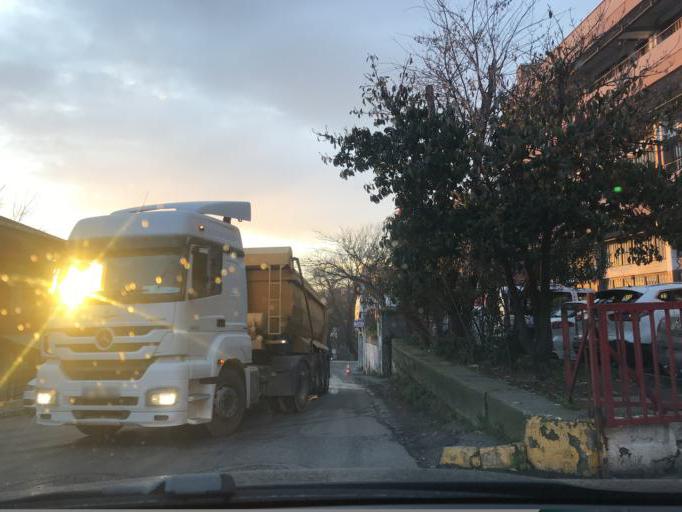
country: TR
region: Istanbul
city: Istanbul
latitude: 41.0391
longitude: 28.9238
